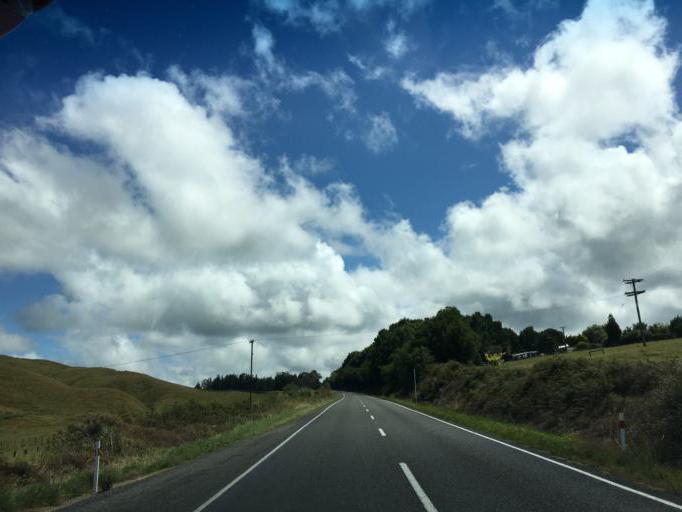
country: NZ
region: Hawke's Bay
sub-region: Wairoa District
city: Wairoa
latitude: -39.0634
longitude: 177.0335
